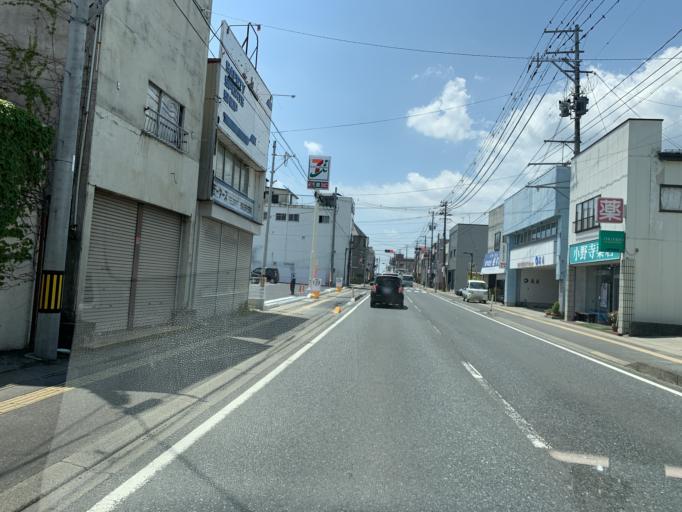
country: JP
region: Miyagi
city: Wakuya
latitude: 38.4766
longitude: 141.0970
